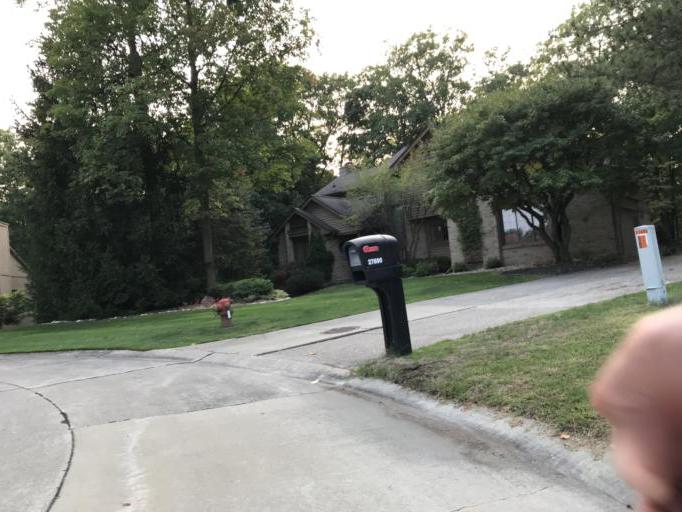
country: US
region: Michigan
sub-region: Oakland County
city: Franklin
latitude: 42.4779
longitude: -83.3213
